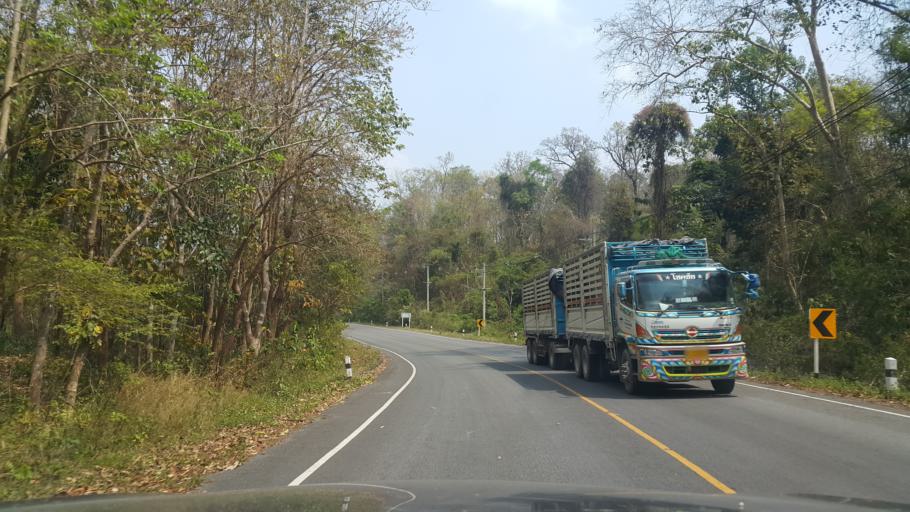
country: TH
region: Lamphun
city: Thung Hua Chang
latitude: 17.9057
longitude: 99.1432
